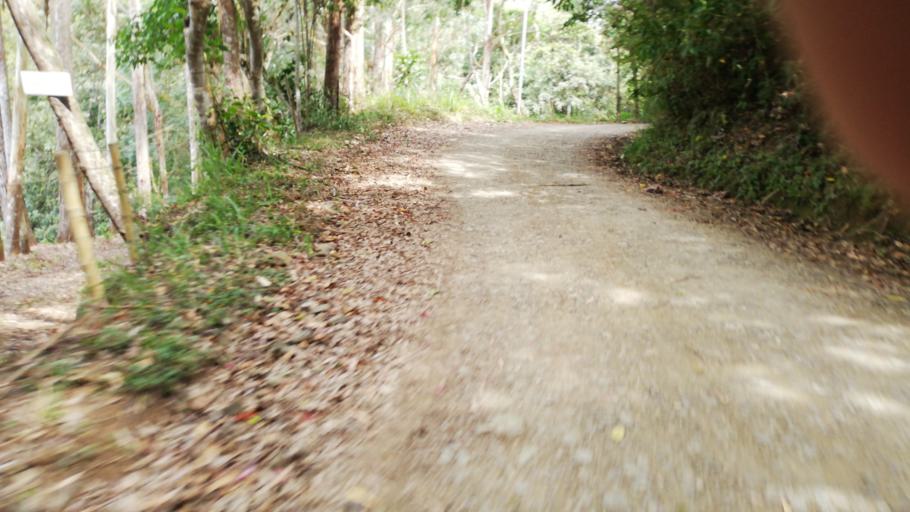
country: CO
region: Valle del Cauca
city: Yumbo
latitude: 3.6282
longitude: -76.5457
